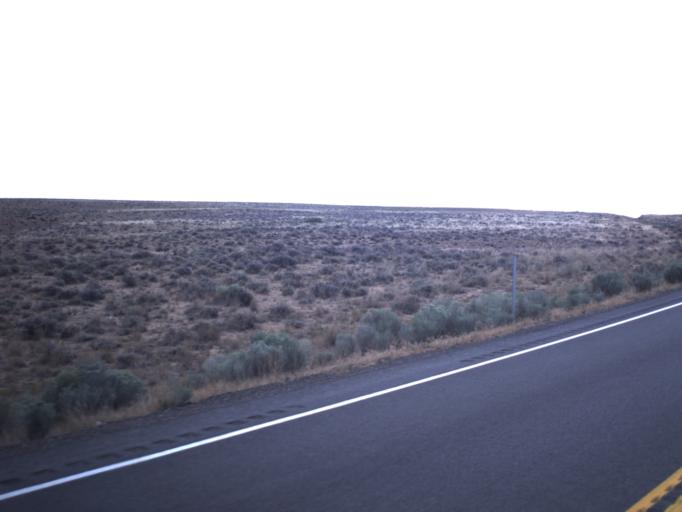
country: US
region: Utah
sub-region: Uintah County
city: Naples
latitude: 40.2761
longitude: -109.4656
